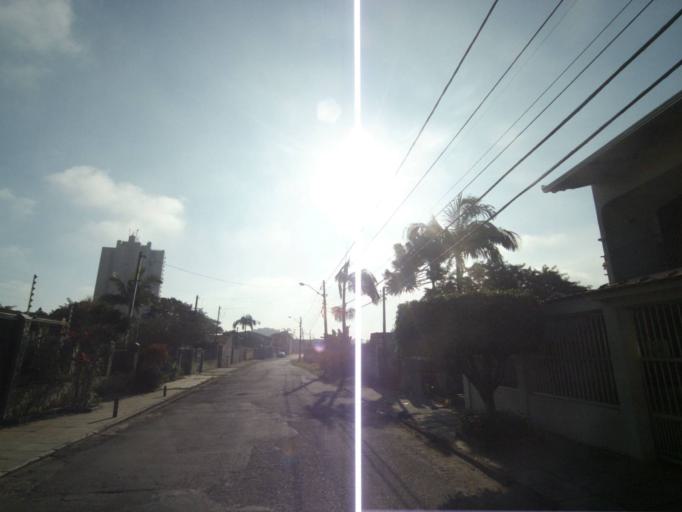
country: BR
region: Parana
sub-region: Paranagua
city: Paranagua
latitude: -25.5210
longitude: -48.5174
